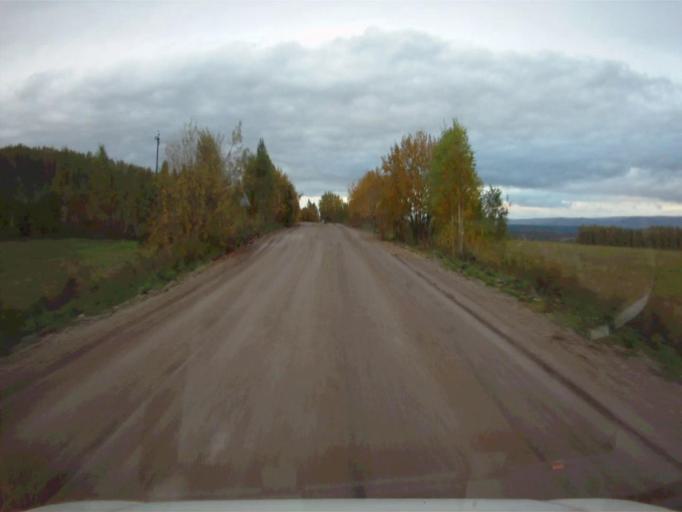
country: RU
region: Sverdlovsk
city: Mikhaylovsk
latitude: 56.1996
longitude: 59.2001
